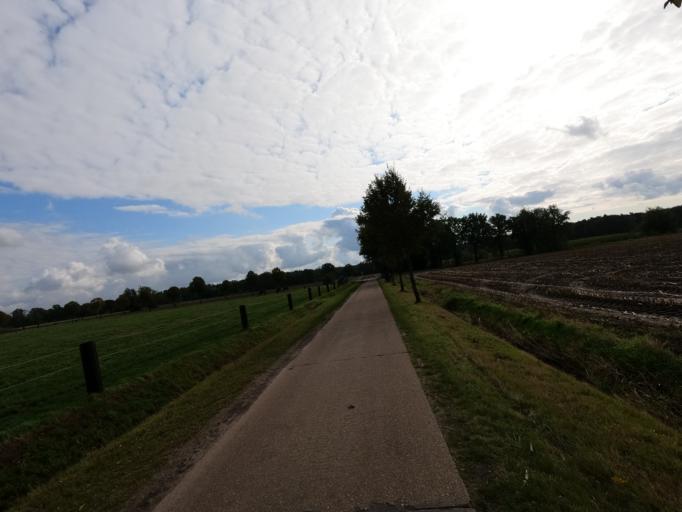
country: BE
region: Flanders
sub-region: Provincie Antwerpen
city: Kasterlee
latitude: 51.2325
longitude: 4.9930
